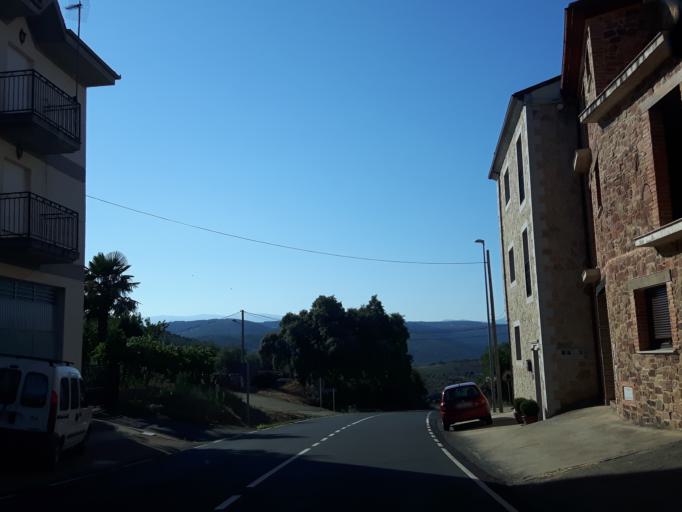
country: ES
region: Castille and Leon
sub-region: Provincia de Salamanca
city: Sotoserrano
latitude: 40.4343
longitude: -6.0305
